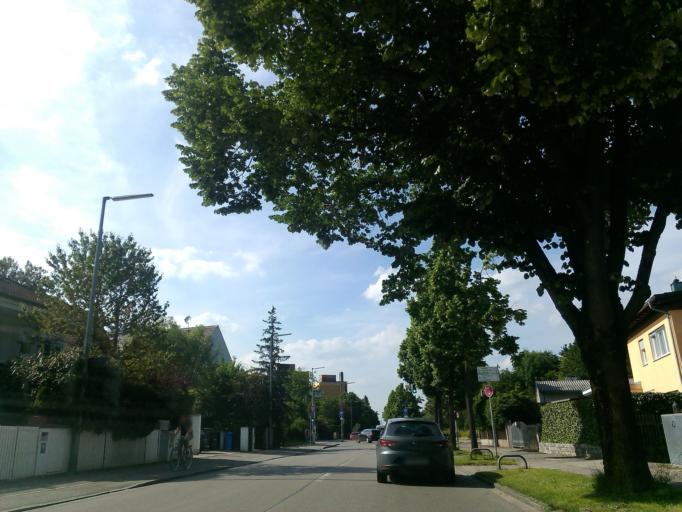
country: DE
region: Bavaria
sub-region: Upper Bavaria
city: Pasing
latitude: 48.1632
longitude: 11.4437
